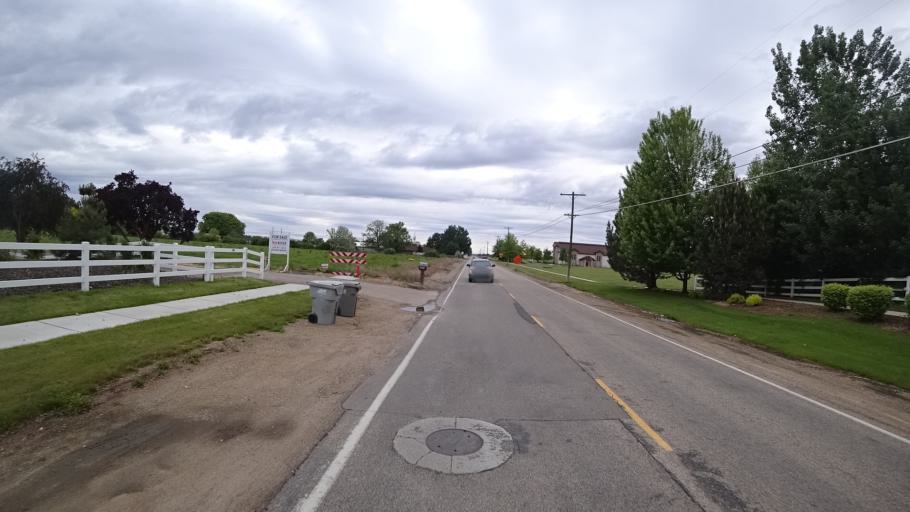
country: US
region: Idaho
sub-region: Ada County
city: Eagle
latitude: 43.7062
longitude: -116.4008
